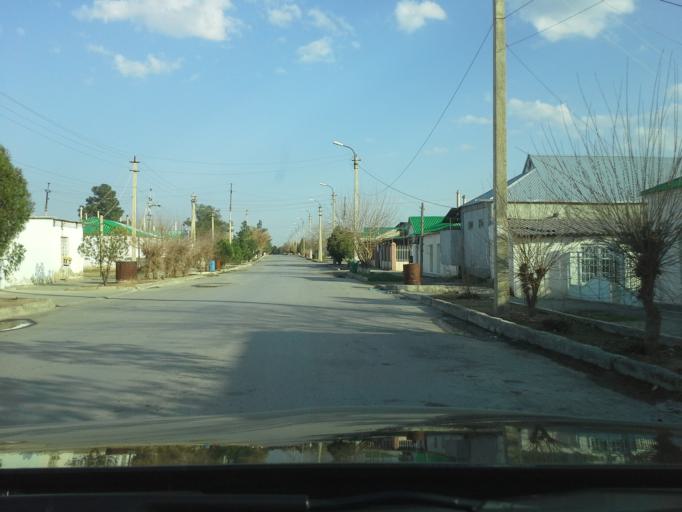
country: TM
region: Ahal
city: Abadan
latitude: 38.0222
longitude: 58.2352
